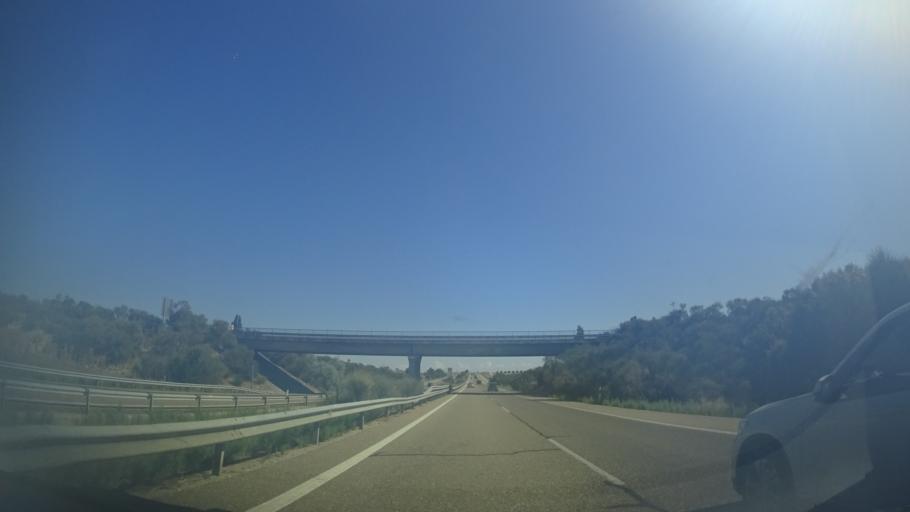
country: ES
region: Castille and Leon
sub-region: Provincia de Valladolid
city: Uruena
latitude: 41.6796
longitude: -5.2078
